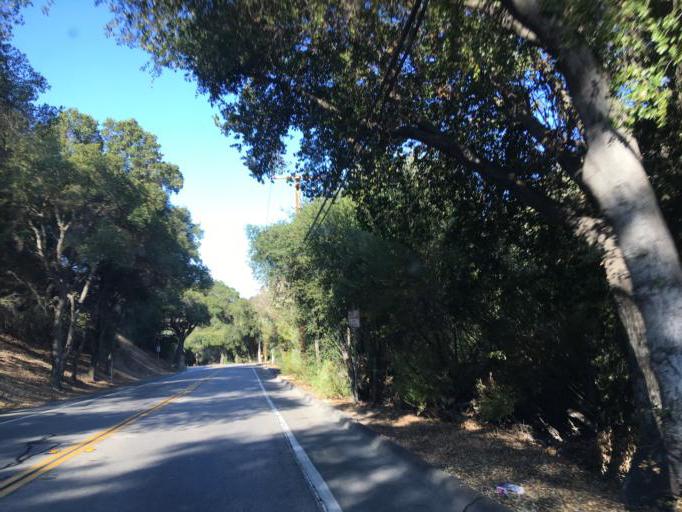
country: US
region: California
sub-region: Los Angeles County
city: Hidden Hills
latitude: 34.1515
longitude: -118.6695
